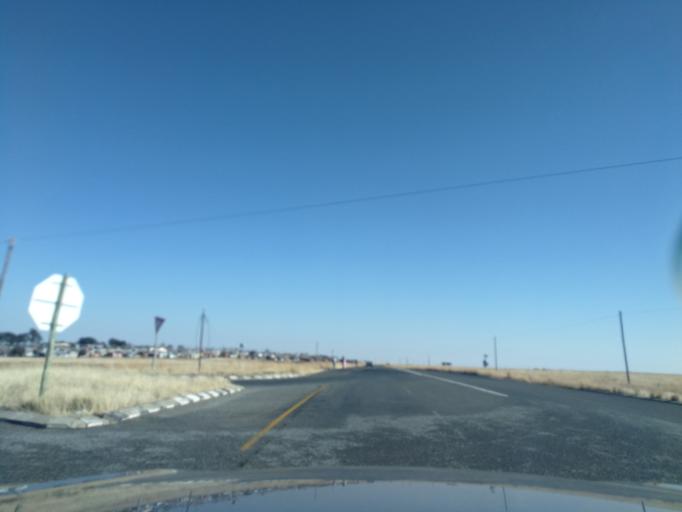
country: ZA
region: Orange Free State
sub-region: Thabo Mofutsanyana District Municipality
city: Senekal
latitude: -27.9417
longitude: 27.5617
